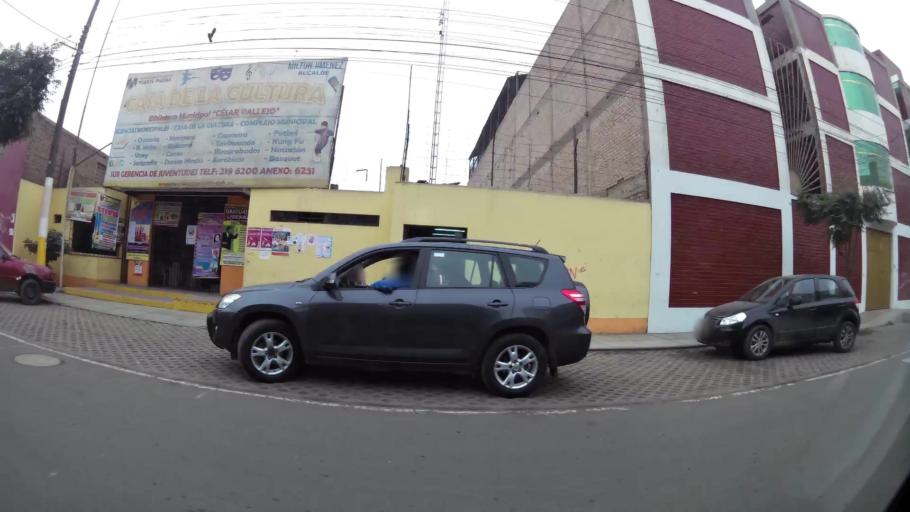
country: PE
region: Lima
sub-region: Lima
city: Carabayllo
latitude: -11.8680
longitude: -77.0752
